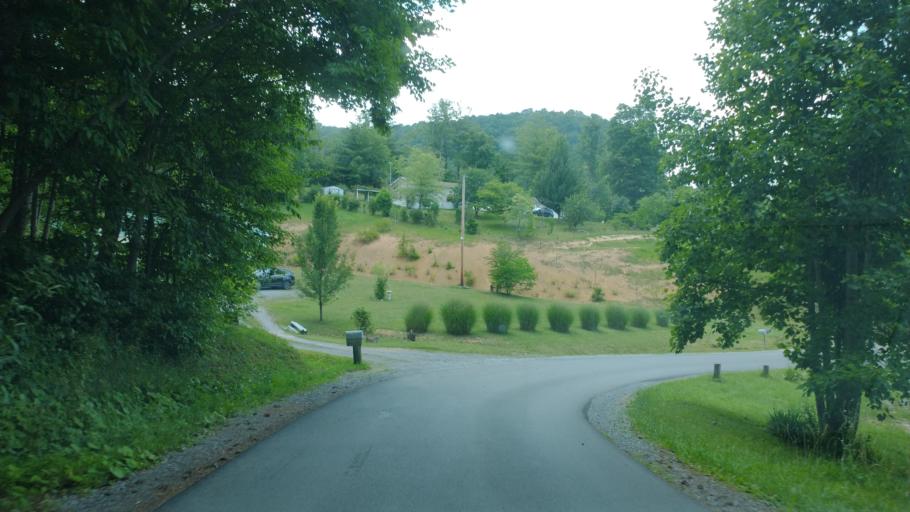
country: US
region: West Virginia
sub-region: Mercer County
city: Athens
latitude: 37.4565
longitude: -81.0624
